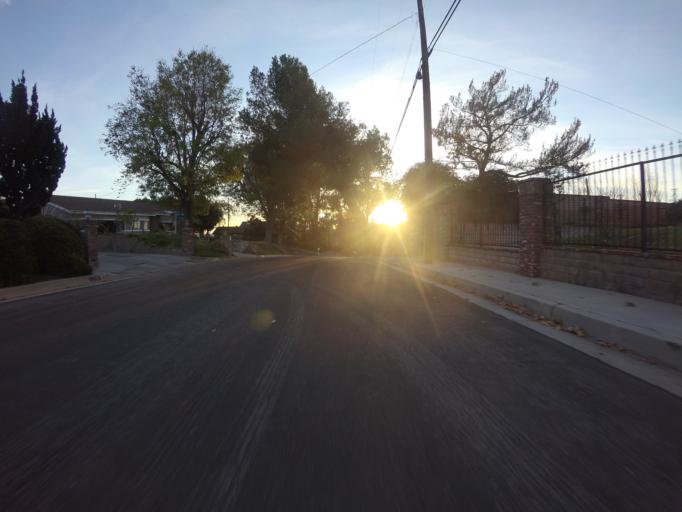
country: US
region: California
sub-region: Los Angeles County
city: San Fernando
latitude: 34.2634
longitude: -118.3511
